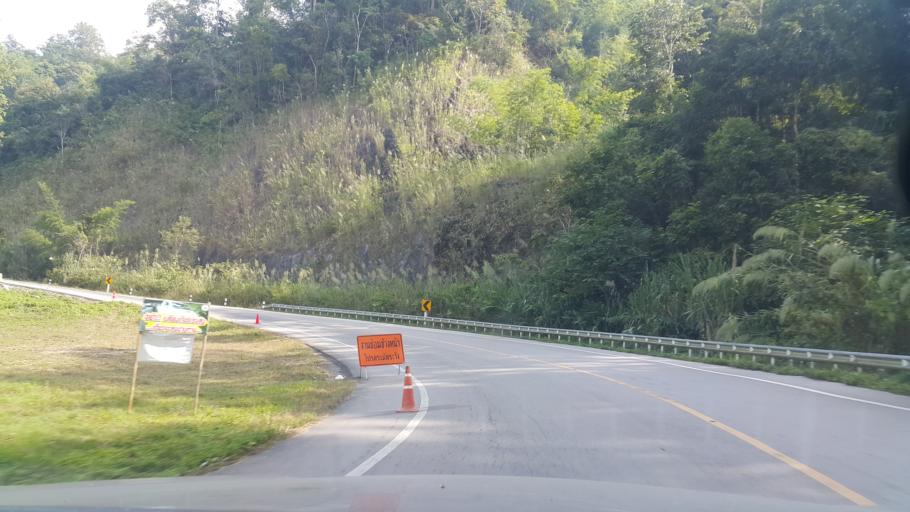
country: TH
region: Lampang
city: Wang Nuea
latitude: 19.0638
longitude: 99.7289
